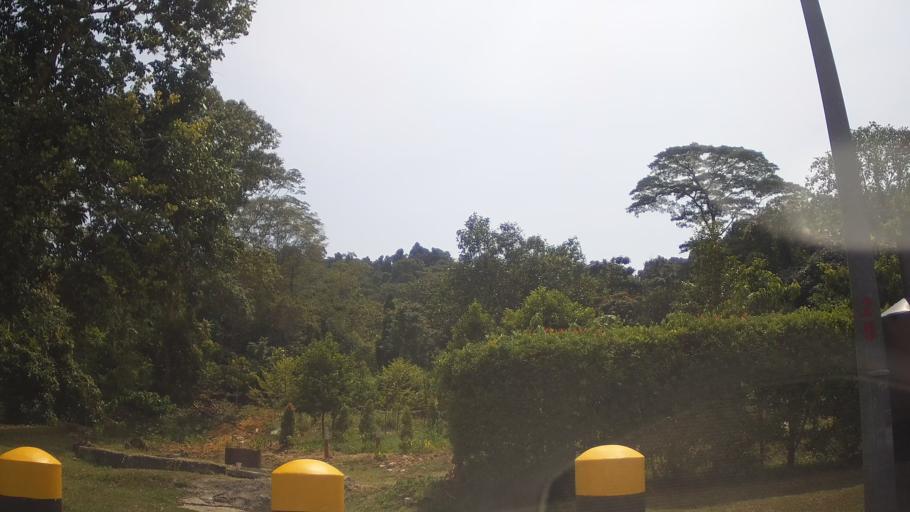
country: SG
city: Singapore
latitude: 1.3576
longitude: 103.7693
